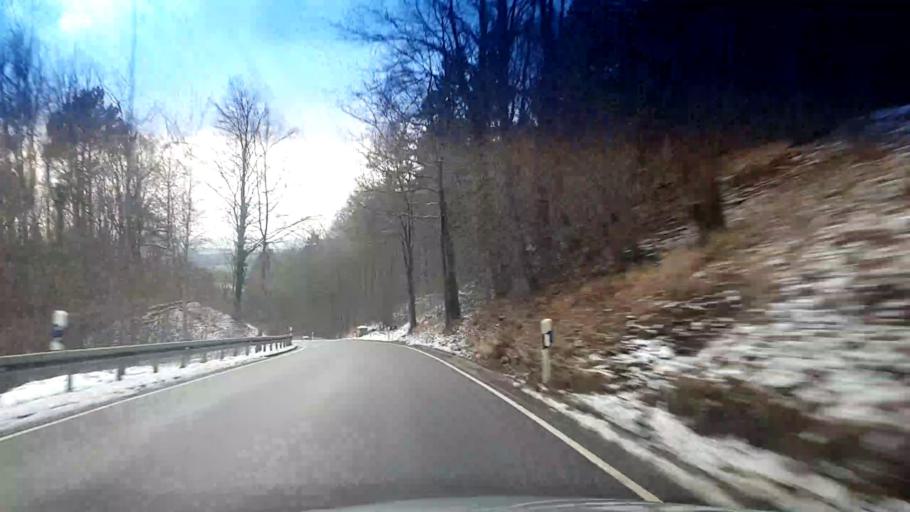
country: DE
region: Bavaria
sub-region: Upper Franconia
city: Poxdorf
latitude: 49.8695
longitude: 11.0795
